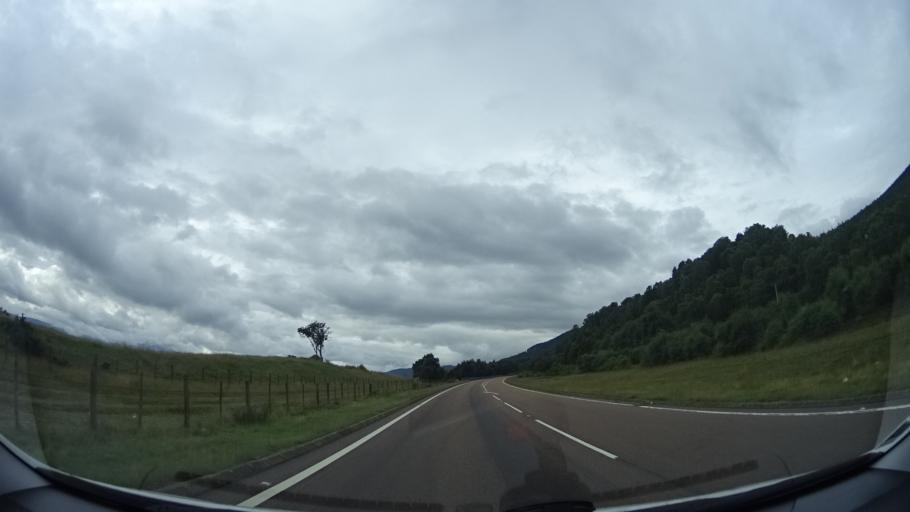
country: GB
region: Scotland
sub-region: Highland
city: Aviemore
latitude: 57.2338
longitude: -3.8104
